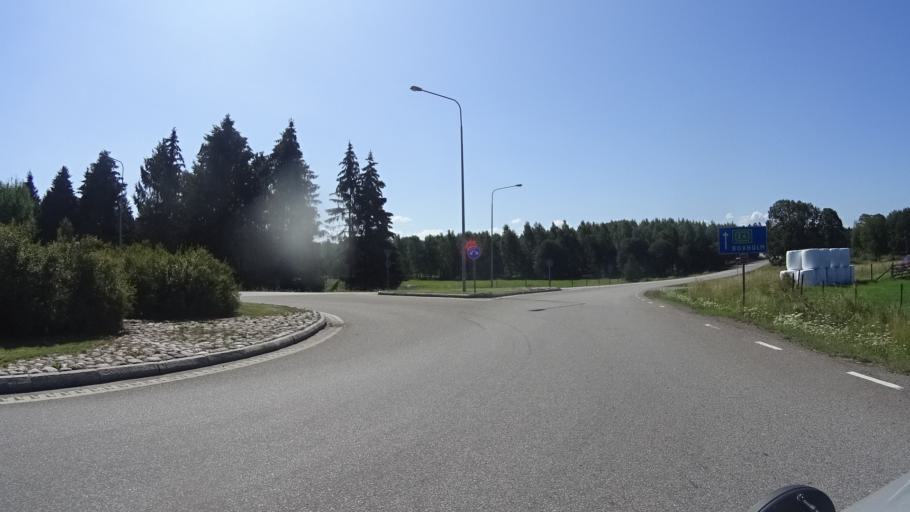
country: SE
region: OEstergoetland
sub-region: Vadstena Kommun
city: Herrestad
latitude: 58.3035
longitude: 14.9208
